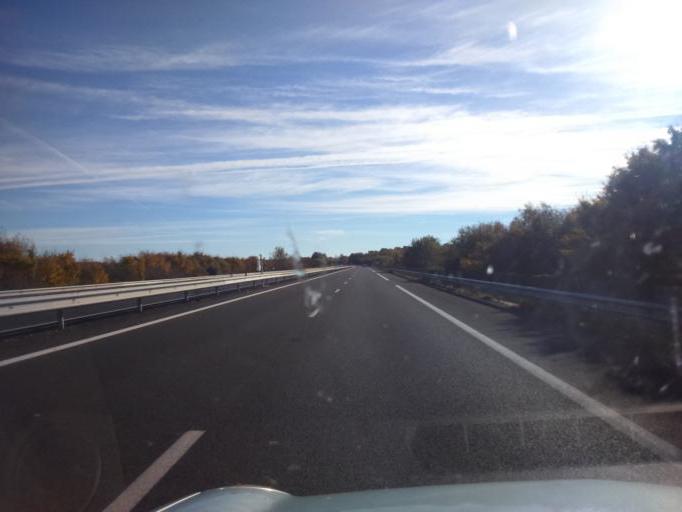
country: FR
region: Poitou-Charentes
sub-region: Departement de la Charente-Maritime
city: Tonnay-Charente
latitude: 45.9561
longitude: -0.9091
